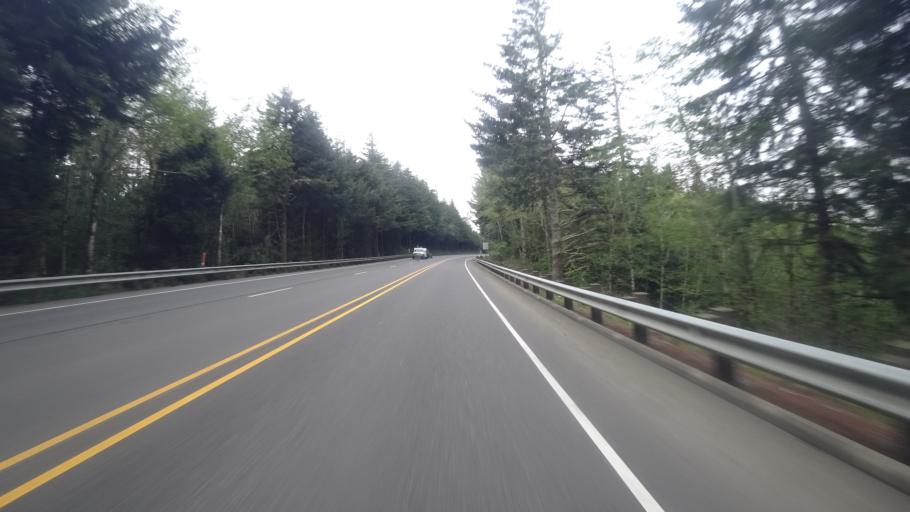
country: US
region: Oregon
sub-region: Coos County
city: Bandon
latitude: 43.1944
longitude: -124.3178
